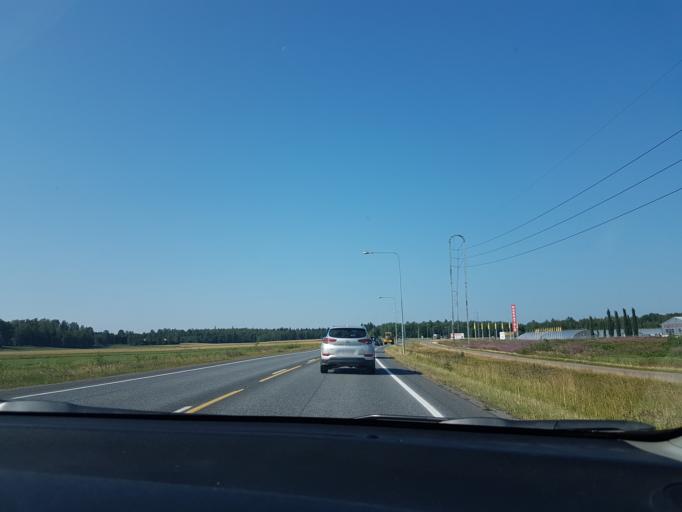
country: FI
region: Uusimaa
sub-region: Helsinki
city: Tuusula
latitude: 60.3745
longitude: 25.0481
